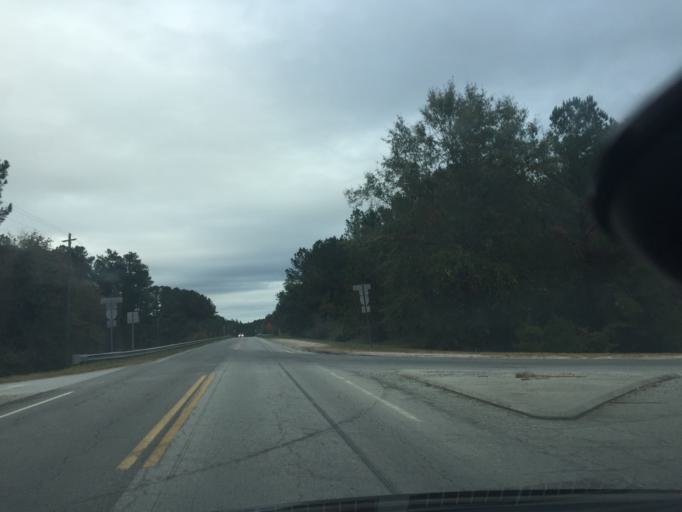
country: US
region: Georgia
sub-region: Chatham County
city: Bloomingdale
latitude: 32.1231
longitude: -81.3879
